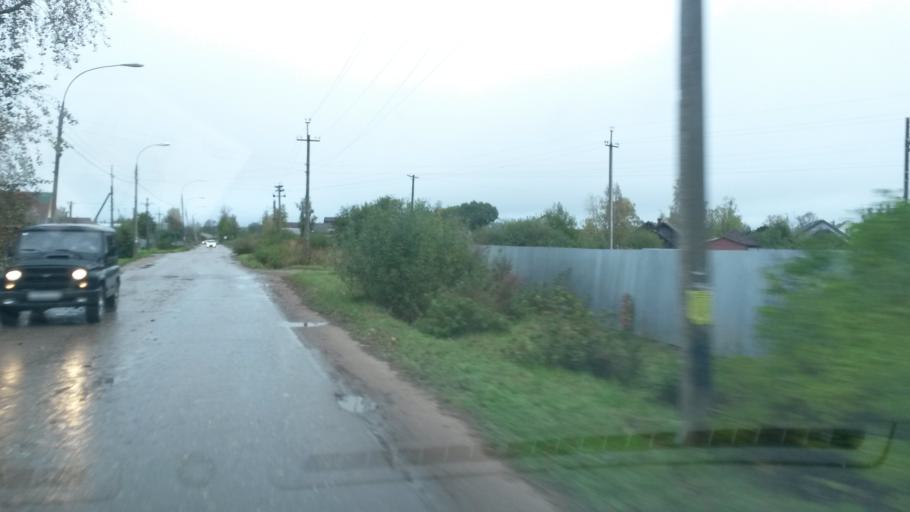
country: RU
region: Jaroslavl
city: Gavrilov-Yam
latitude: 57.3114
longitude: 39.8584
